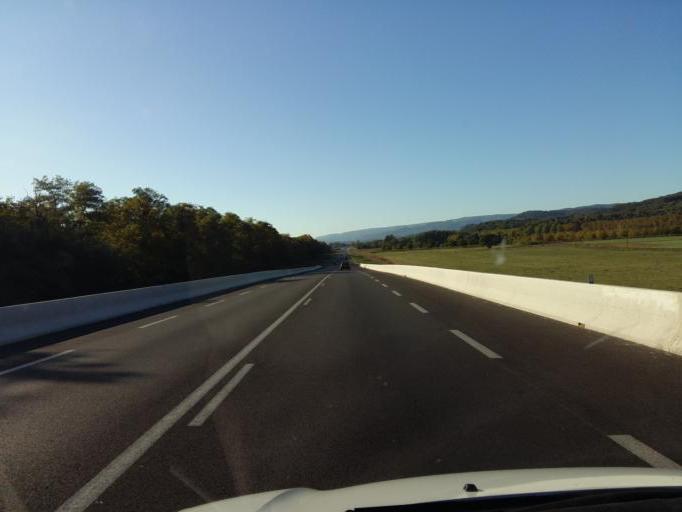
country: FR
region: Provence-Alpes-Cote d'Azur
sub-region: Departement du Vaucluse
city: Villelaure
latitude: 43.7138
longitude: 5.4107
